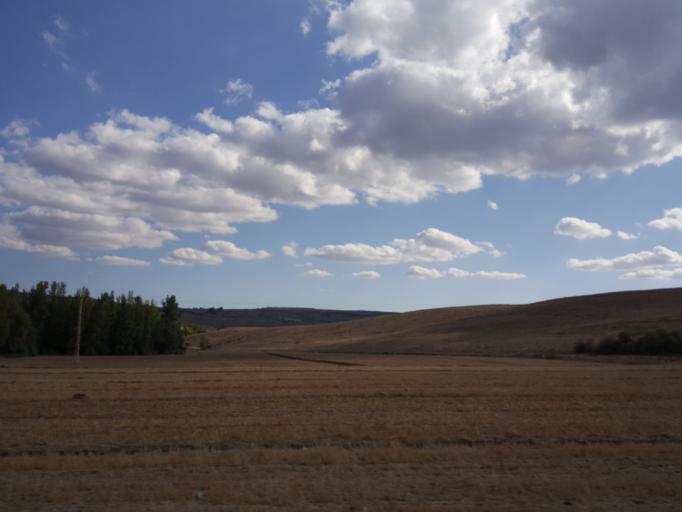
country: TR
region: Tokat
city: Sulusaray
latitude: 39.9765
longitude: 36.0160
